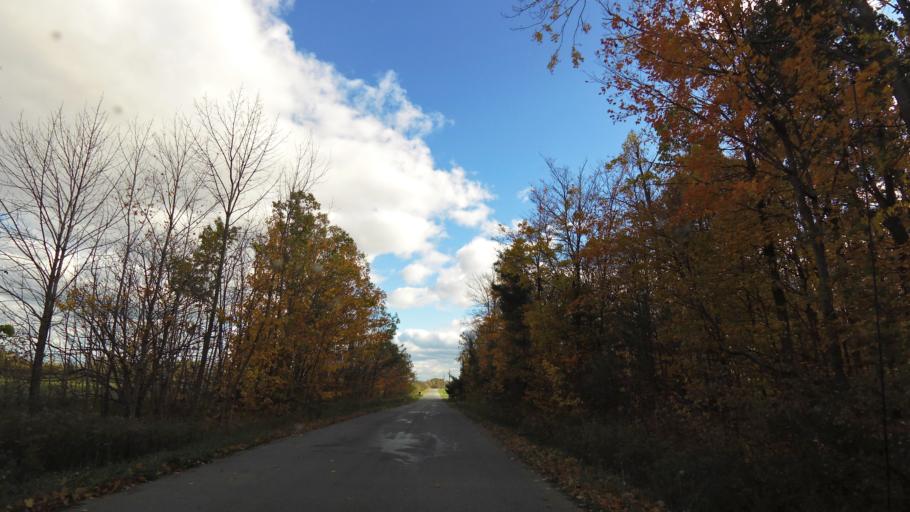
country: CA
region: Ontario
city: Burlington
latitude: 43.4450
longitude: -79.8494
